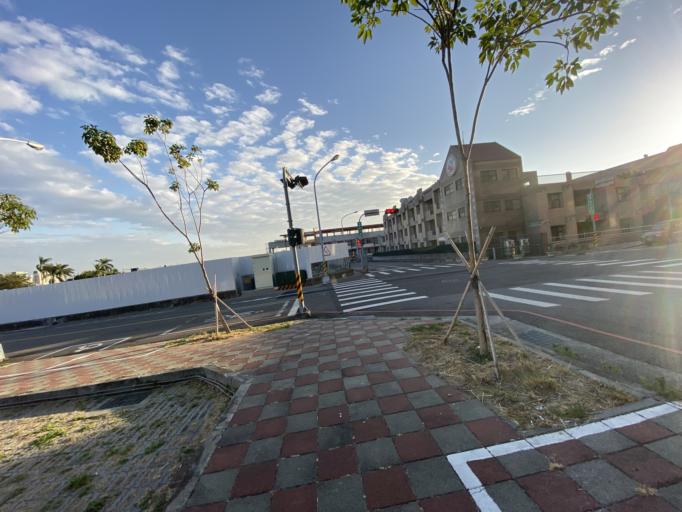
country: TW
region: Taiwan
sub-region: Changhua
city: Chang-hua
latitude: 24.1358
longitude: 120.6075
